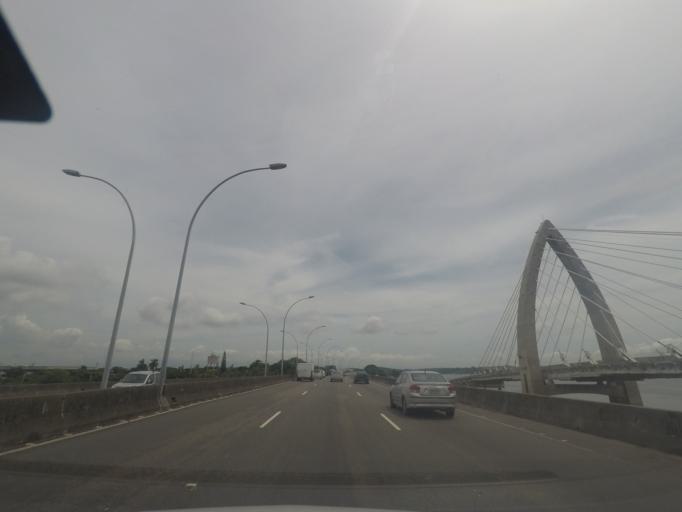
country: BR
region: Rio de Janeiro
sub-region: Rio De Janeiro
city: Rio de Janeiro
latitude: -22.8358
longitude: -43.2409
